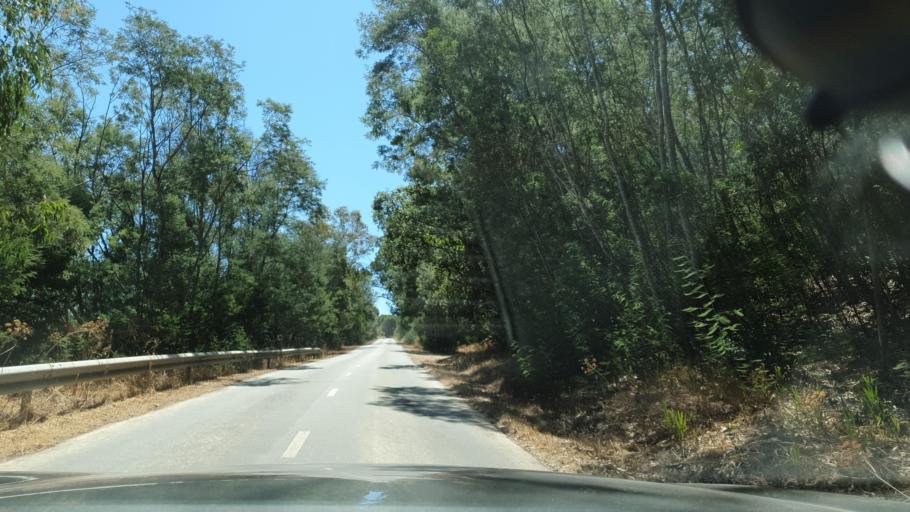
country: PT
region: Beja
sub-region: Odemira
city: Odemira
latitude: 37.5069
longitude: -8.4389
